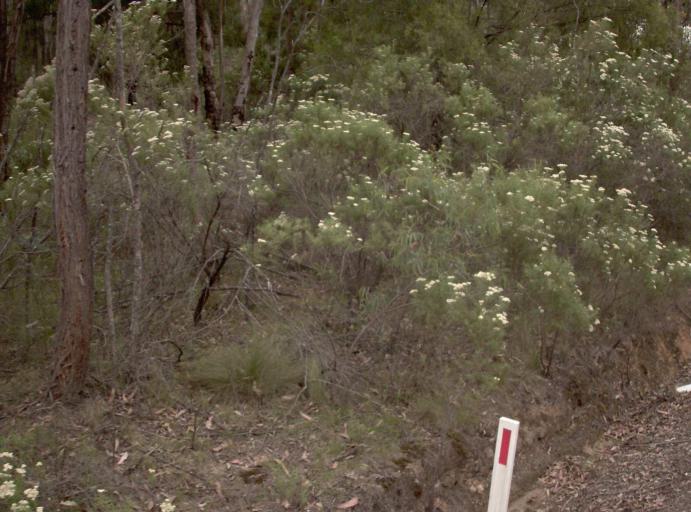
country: AU
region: Victoria
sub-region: East Gippsland
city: Bairnsdale
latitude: -37.6524
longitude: 147.2784
